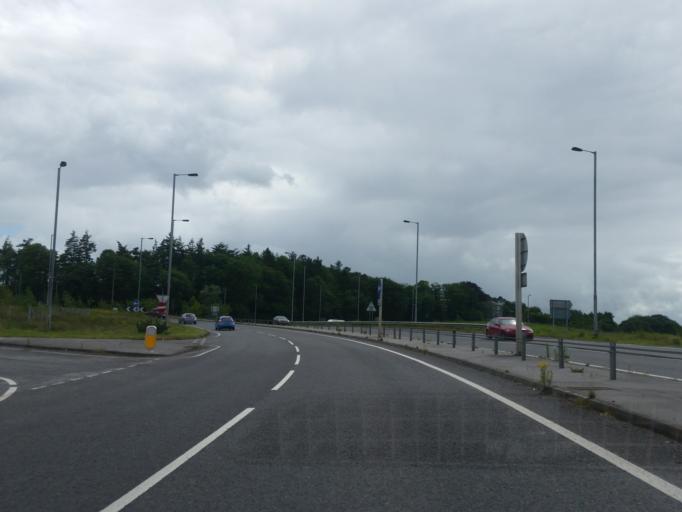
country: IE
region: Ulster
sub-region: County Monaghan
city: Monaghan
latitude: 54.4566
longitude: -7.0329
